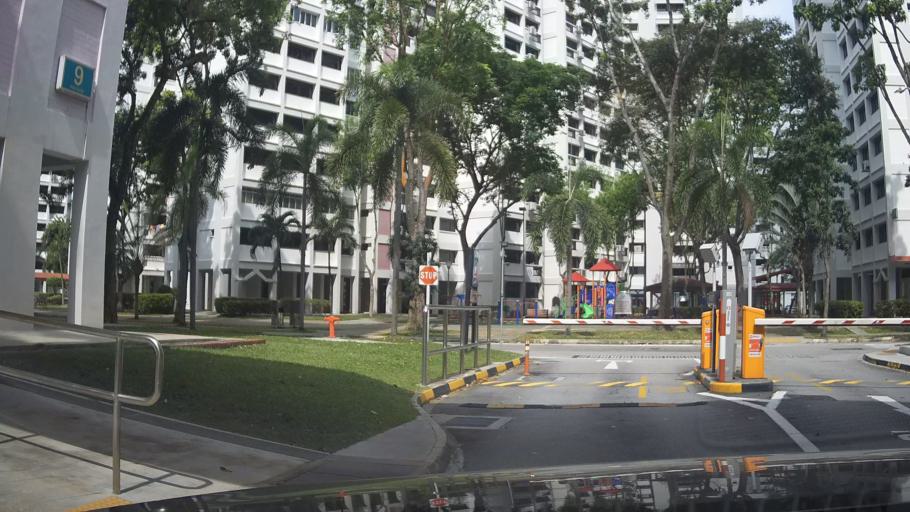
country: SG
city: Singapore
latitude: 1.3088
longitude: 103.8826
